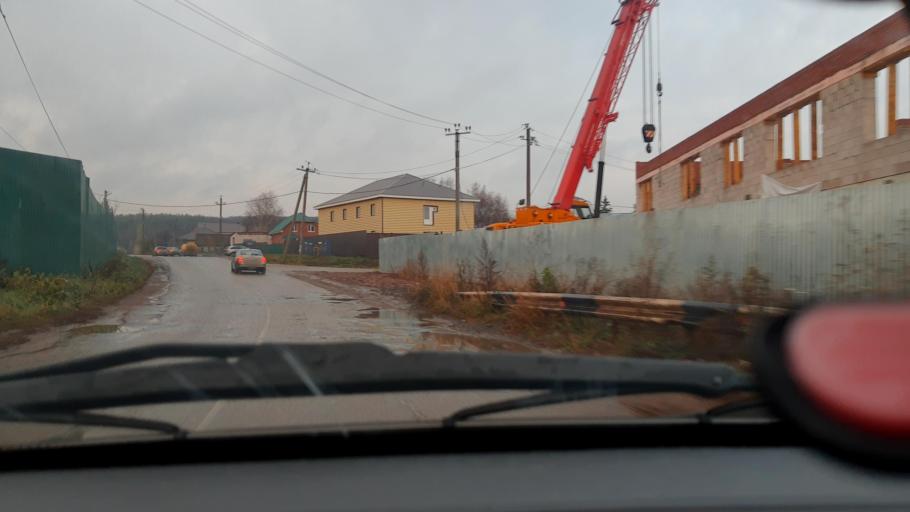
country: RU
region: Bashkortostan
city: Mikhaylovka
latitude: 54.8019
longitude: 55.8805
